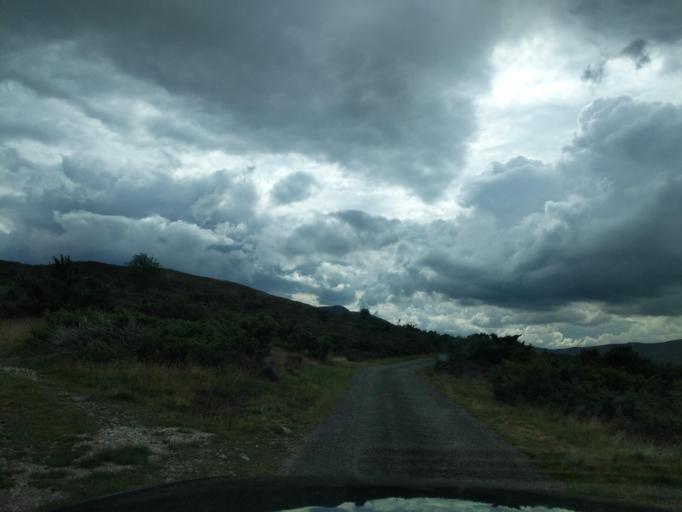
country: GB
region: Scotland
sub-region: Highland
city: Aviemore
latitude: 57.2582
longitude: -3.8940
